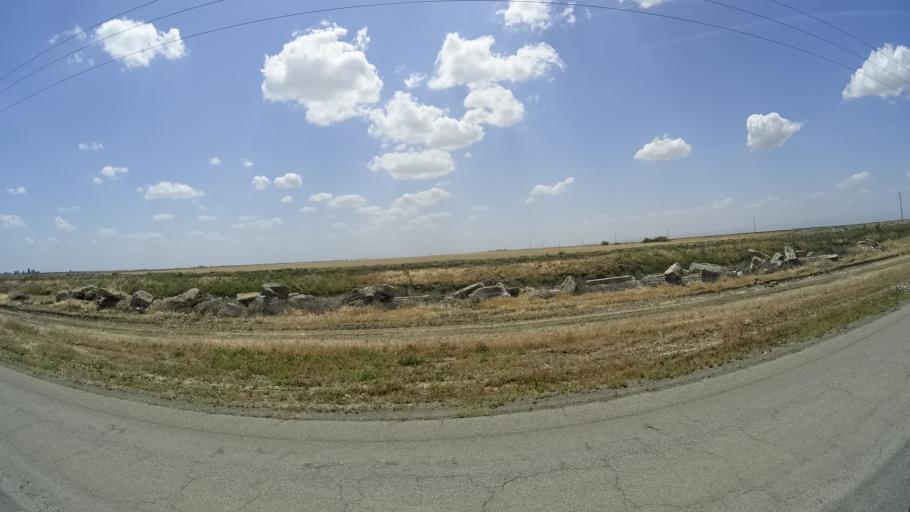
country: US
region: California
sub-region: Kings County
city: Stratford
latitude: 36.1895
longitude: -119.8769
